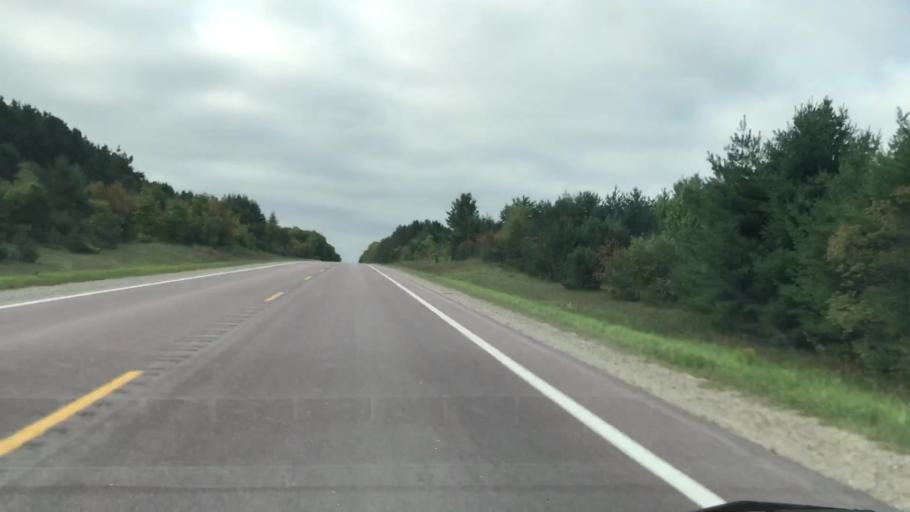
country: US
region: Michigan
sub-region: Luce County
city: Newberry
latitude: 46.2862
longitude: -85.5704
